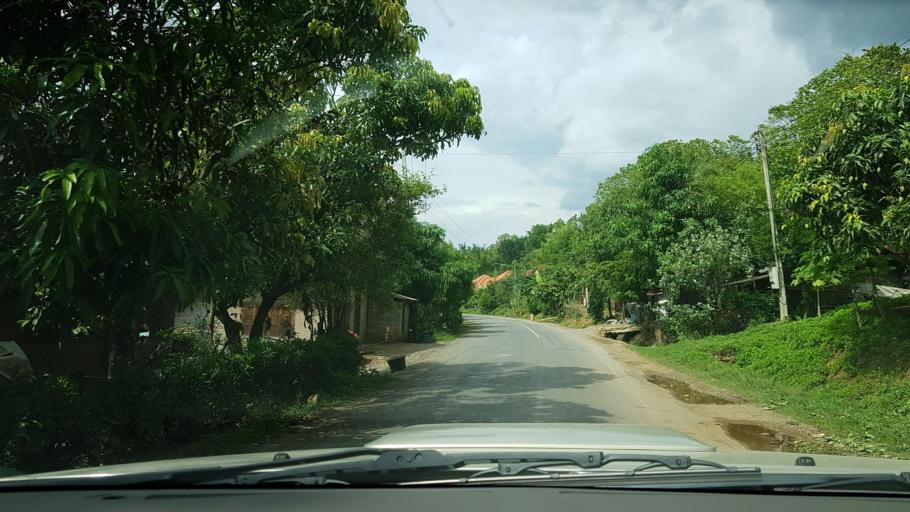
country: LA
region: Loungnamtha
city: Muang Nale
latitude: 20.3166
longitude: 101.6567
